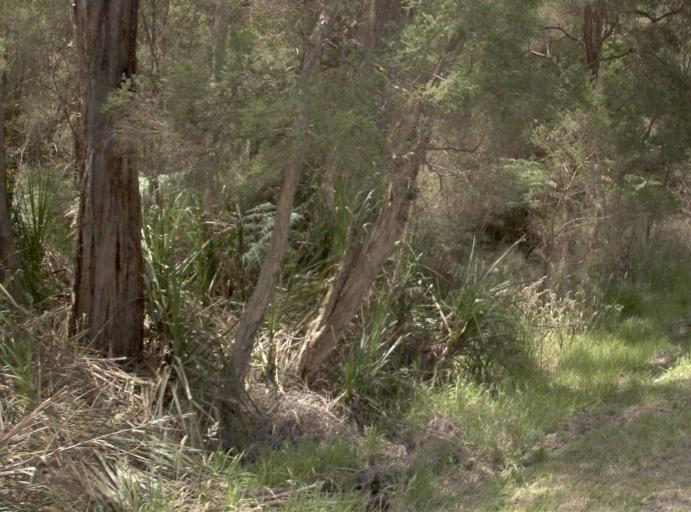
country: AU
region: Victoria
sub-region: Bass Coast
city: North Wonthaggi
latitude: -38.7316
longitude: 146.1236
